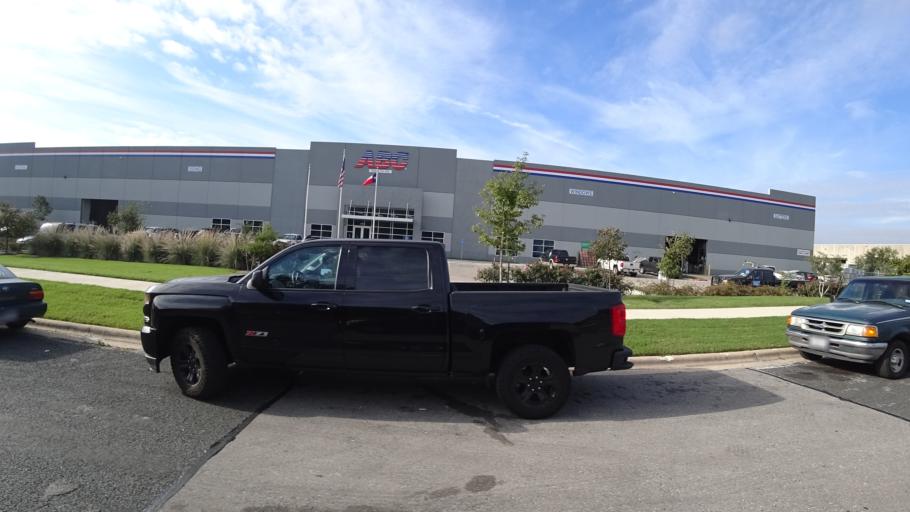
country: US
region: Texas
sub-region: Travis County
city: Austin
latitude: 30.2069
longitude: -97.7321
